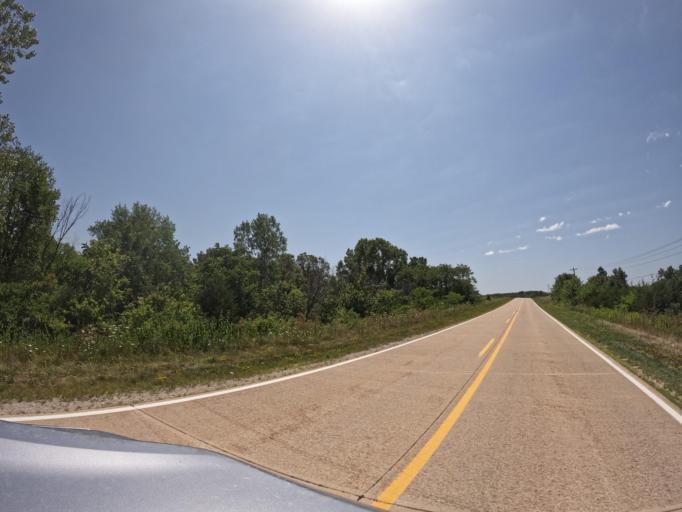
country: US
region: Iowa
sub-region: Henry County
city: Mount Pleasant
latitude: 40.9227
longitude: -91.5540
